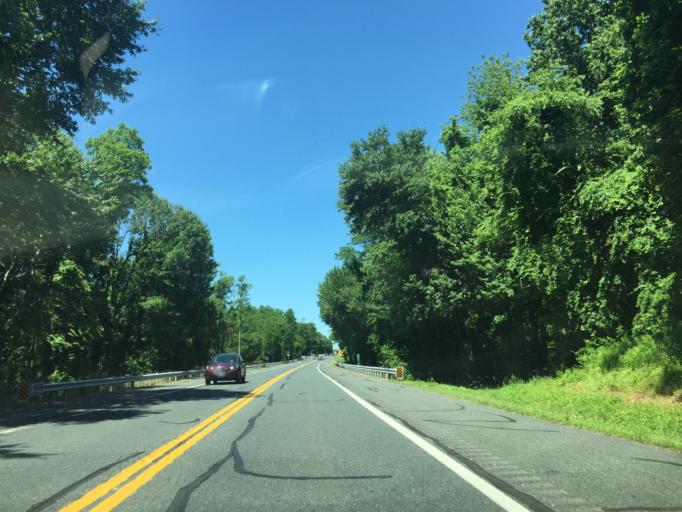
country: US
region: Maryland
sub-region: Harford County
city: Bel Air North
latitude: 39.5740
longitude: -76.4193
